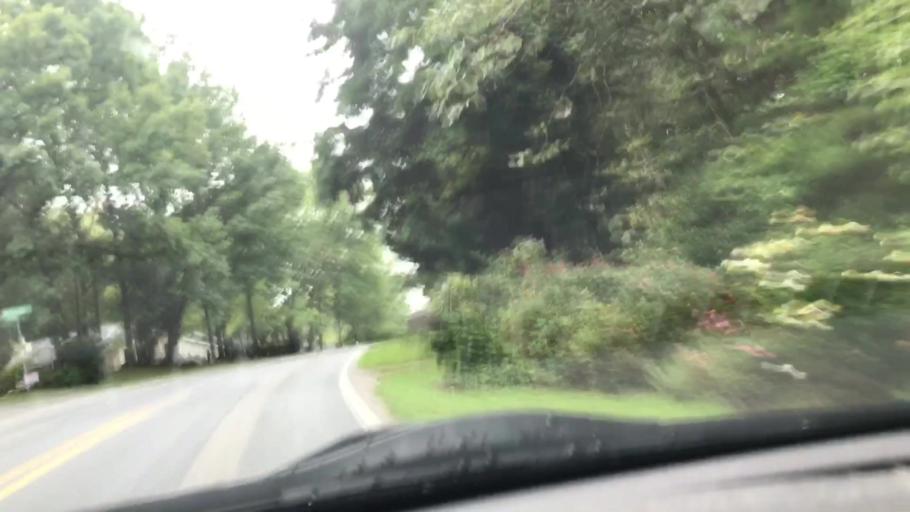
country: US
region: North Carolina
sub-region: Randolph County
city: Asheboro
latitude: 35.7238
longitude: -79.8010
